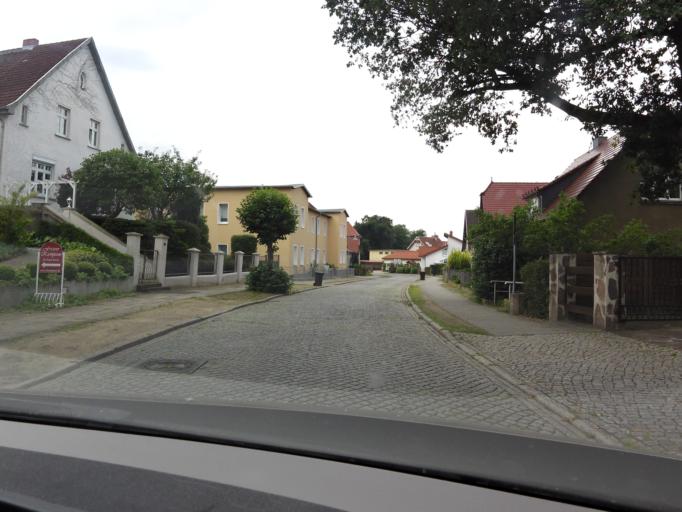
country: DE
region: Mecklenburg-Vorpommern
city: Neustrelitz
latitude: 53.3646
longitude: 13.0763
